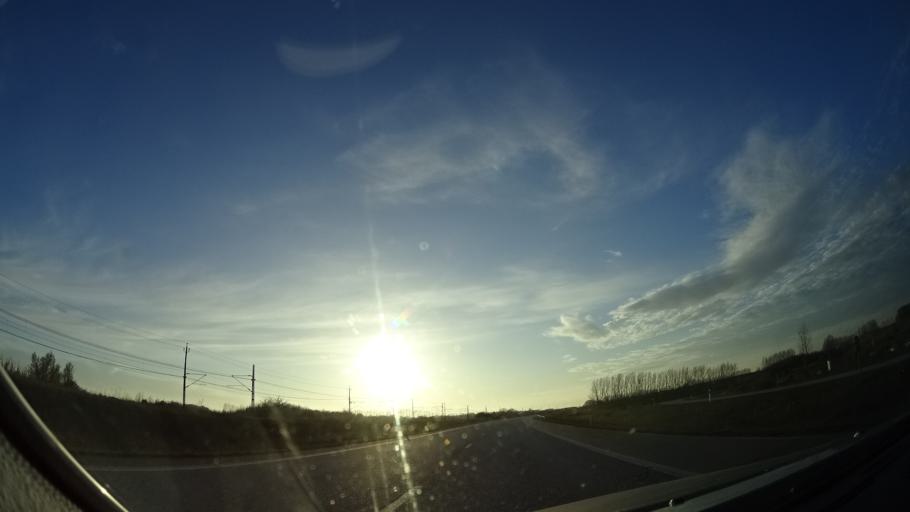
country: SE
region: Skane
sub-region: Malmo
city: Bunkeflostrand
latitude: 55.5496
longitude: 12.9570
